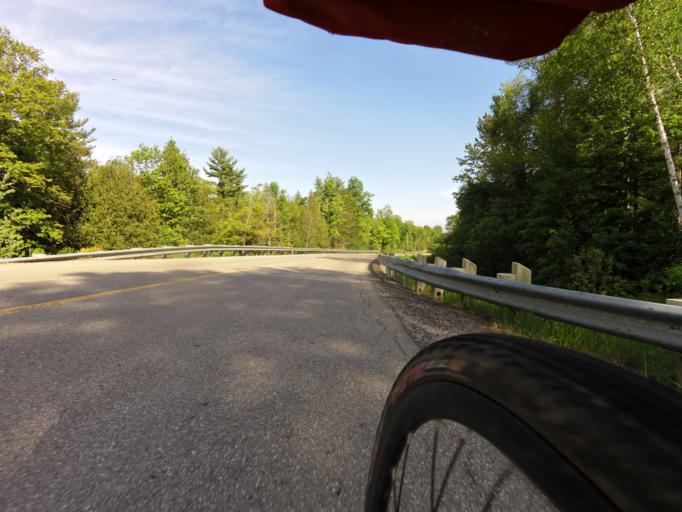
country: CA
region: Ontario
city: Arnprior
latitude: 45.1705
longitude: -76.4896
